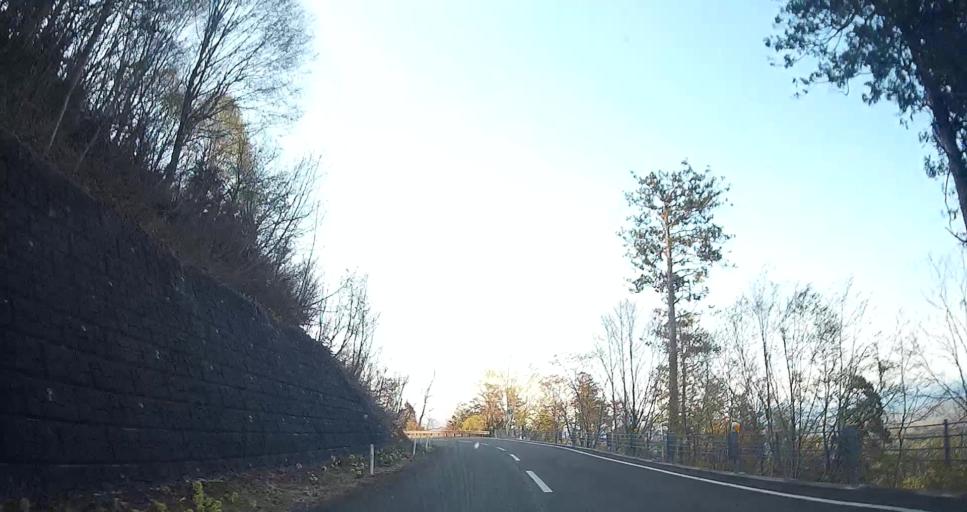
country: JP
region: Aomori
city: Mutsu
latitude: 41.3110
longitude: 141.1129
